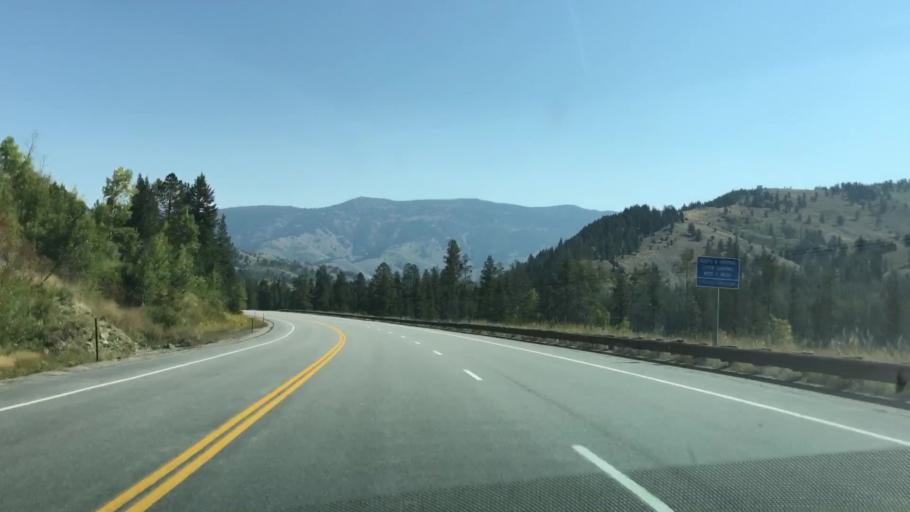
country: US
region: Wyoming
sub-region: Teton County
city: Hoback
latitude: 43.2052
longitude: -110.8256
